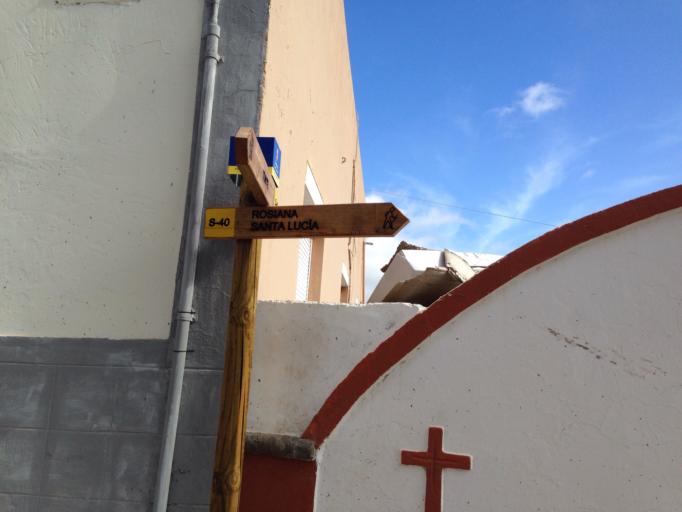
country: ES
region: Canary Islands
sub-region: Provincia de Las Palmas
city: San Bartolome
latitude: 27.9247
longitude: -15.5721
